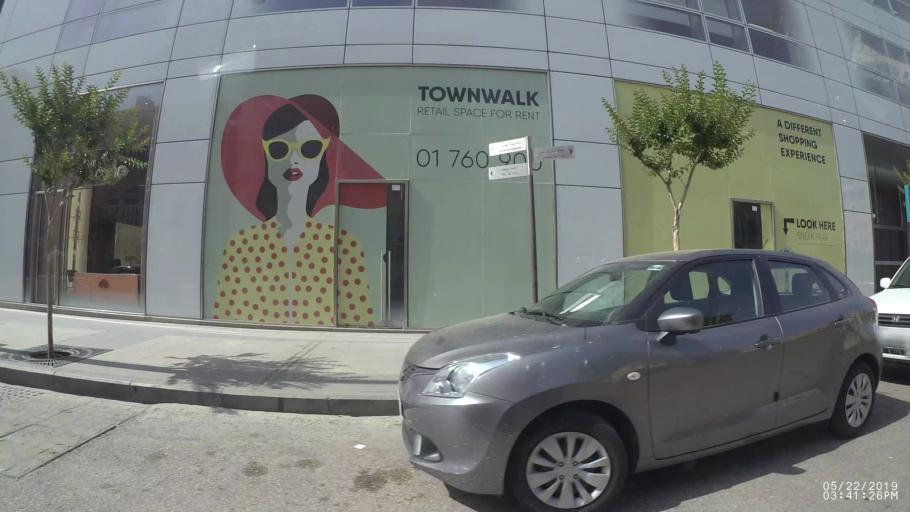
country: LB
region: Beyrouth
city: Beirut
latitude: 33.8989
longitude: 35.5000
